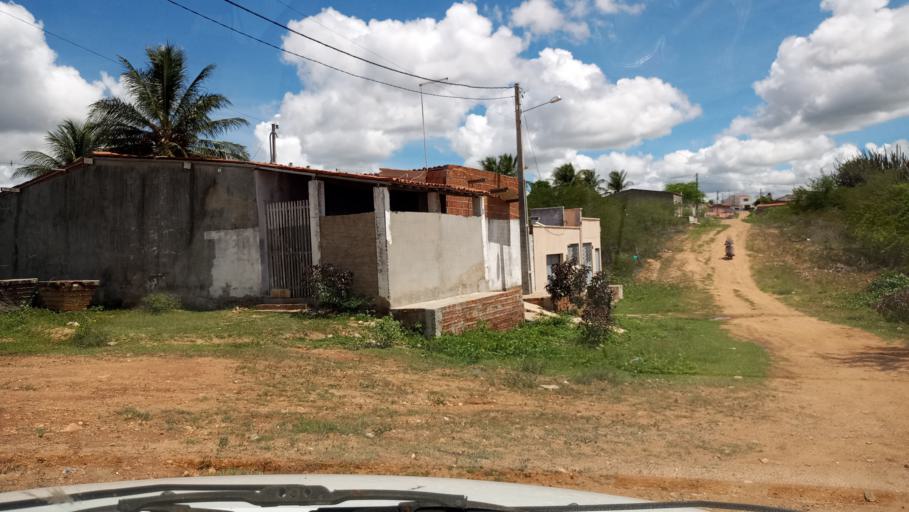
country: BR
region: Rio Grande do Norte
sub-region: Sao Paulo Do Potengi
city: Sao Paulo do Potengi
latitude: -5.9041
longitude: -35.7722
